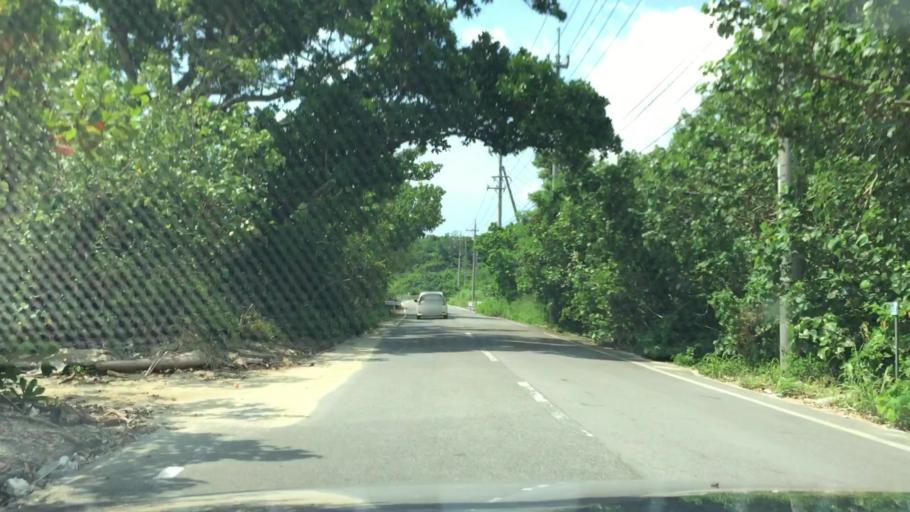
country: JP
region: Okinawa
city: Ishigaki
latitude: 24.4656
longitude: 124.2264
